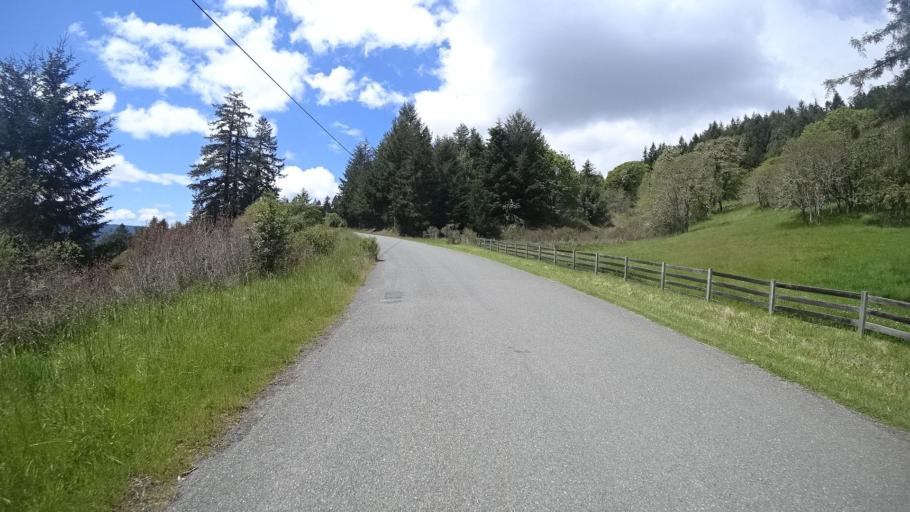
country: US
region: California
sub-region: Humboldt County
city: Blue Lake
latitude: 40.8436
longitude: -123.9018
